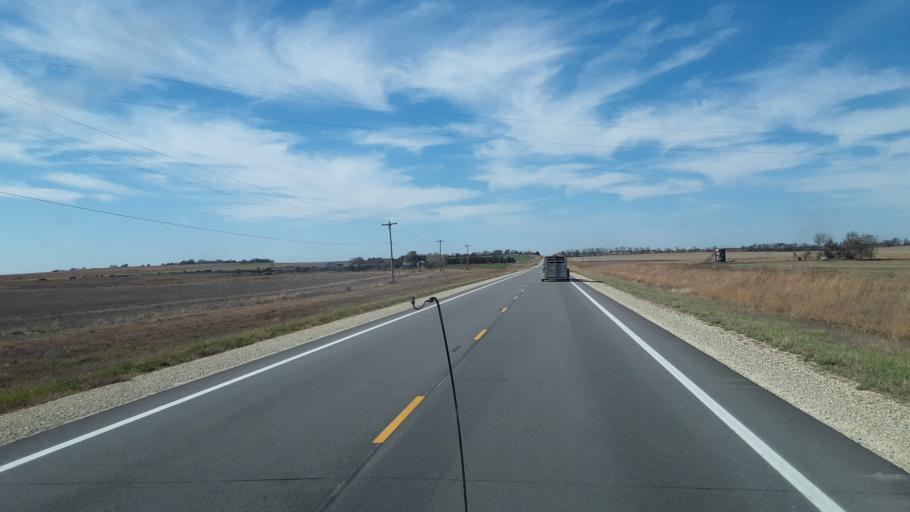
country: US
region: Kansas
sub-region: Marion County
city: Marion
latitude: 38.3629
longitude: -96.9267
